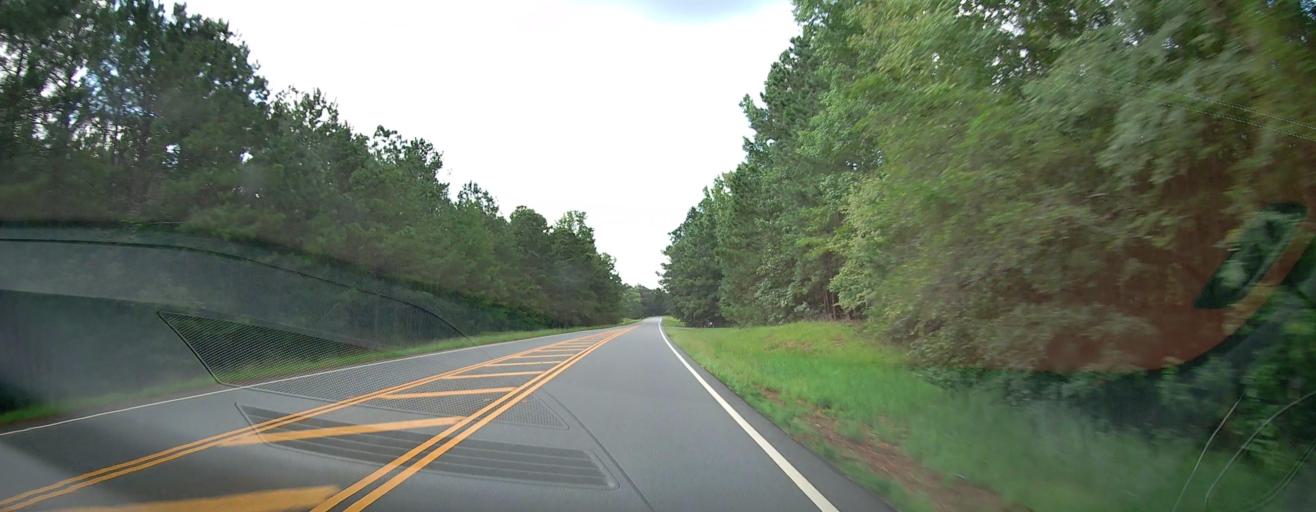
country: US
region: Georgia
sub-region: Bibb County
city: West Point
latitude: 32.8745
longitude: -83.9219
